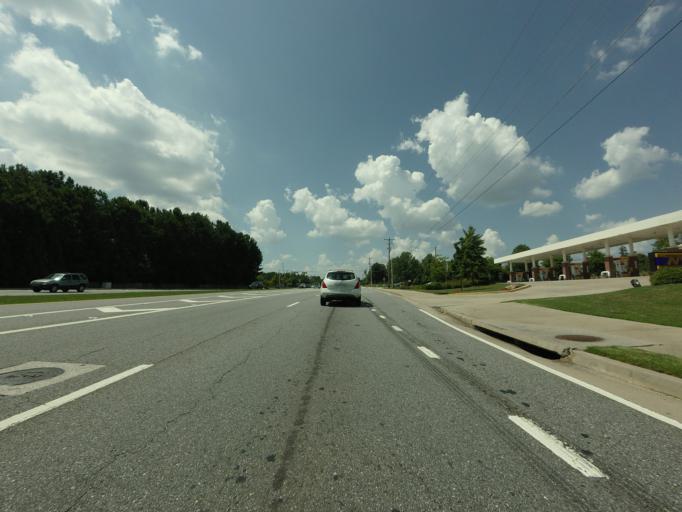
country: US
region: Georgia
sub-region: Fulton County
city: Johns Creek
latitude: 34.0399
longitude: -84.2191
